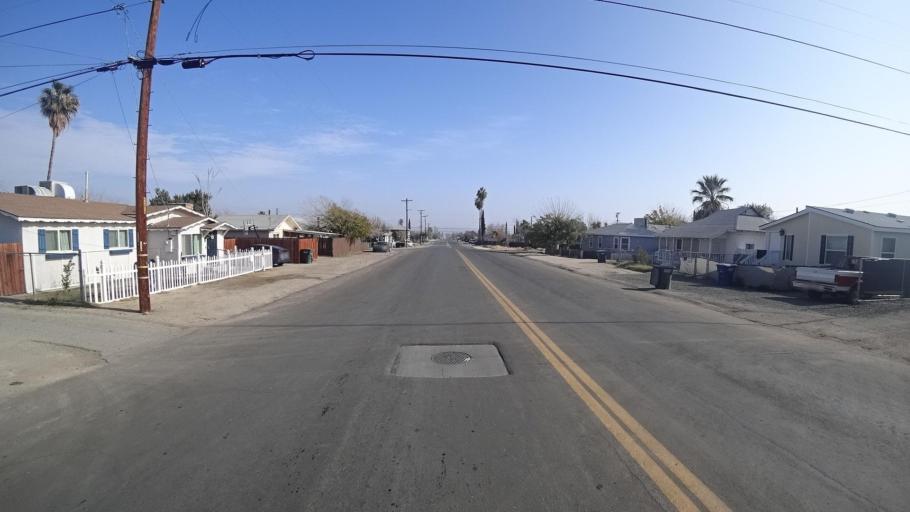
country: US
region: California
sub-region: Kern County
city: Ford City
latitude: 35.1546
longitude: -119.4545
